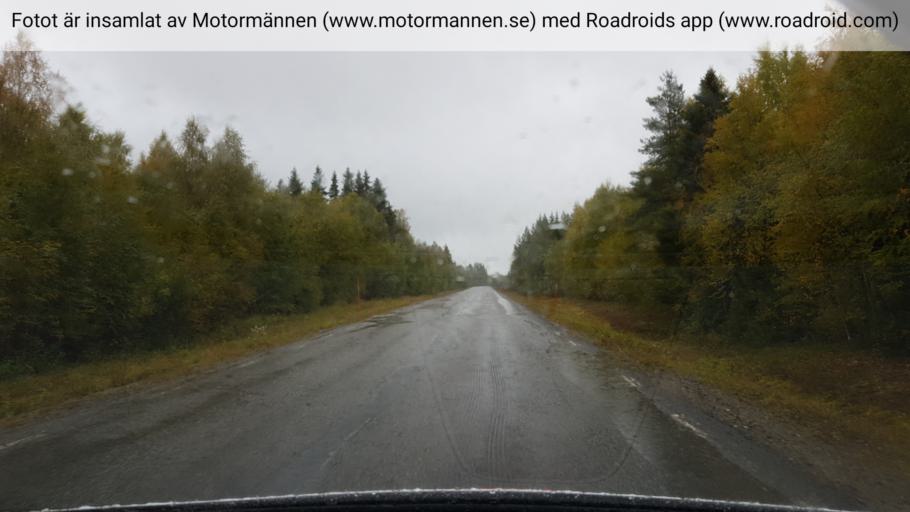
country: SE
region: Vaesterbotten
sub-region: Vannas Kommun
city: Vannasby
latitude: 64.0344
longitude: 19.9329
